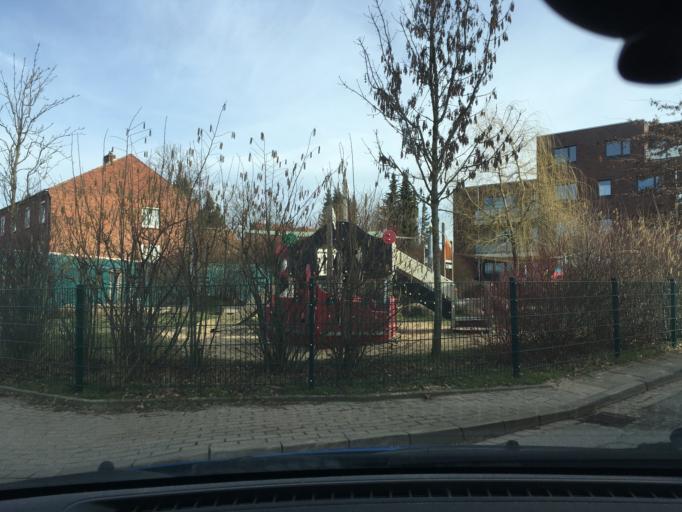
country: DE
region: Lower Saxony
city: Lueneburg
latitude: 53.2472
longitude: 10.4275
